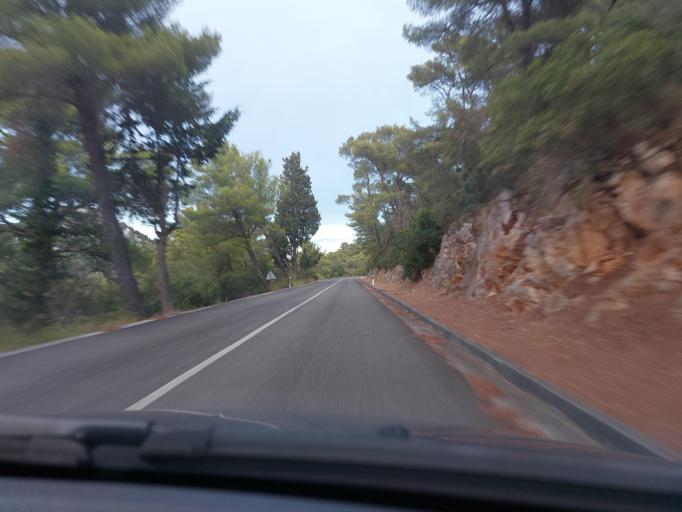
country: HR
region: Dubrovacko-Neretvanska
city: Smokvica
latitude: 42.7695
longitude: 16.8551
